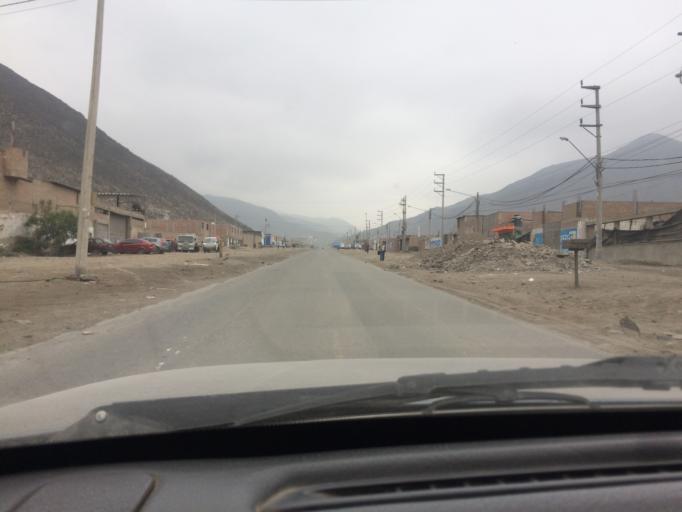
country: PE
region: Lima
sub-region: Lima
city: Cieneguilla
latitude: -12.1664
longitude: -76.8653
